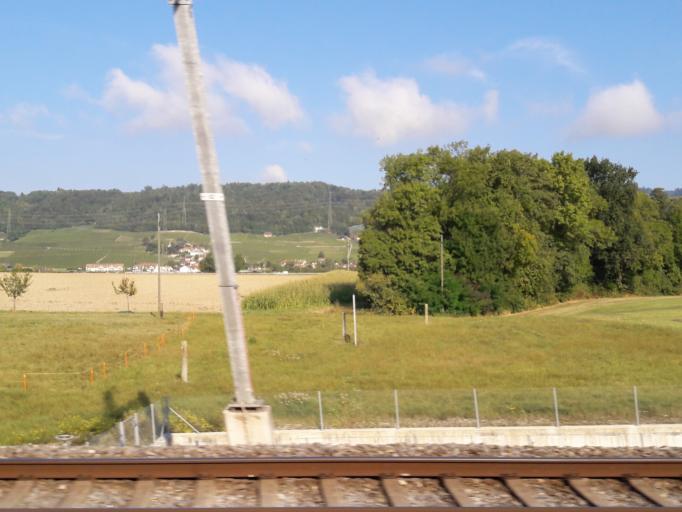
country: CH
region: Vaud
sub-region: Nyon District
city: Gland
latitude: 46.4396
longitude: 6.2913
